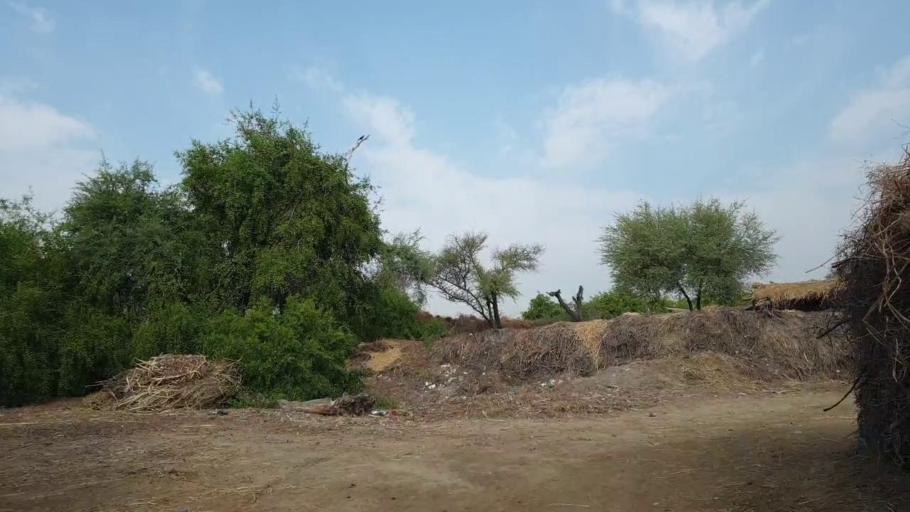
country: PK
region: Sindh
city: Tando Muhammad Khan
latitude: 25.0244
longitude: 68.4548
